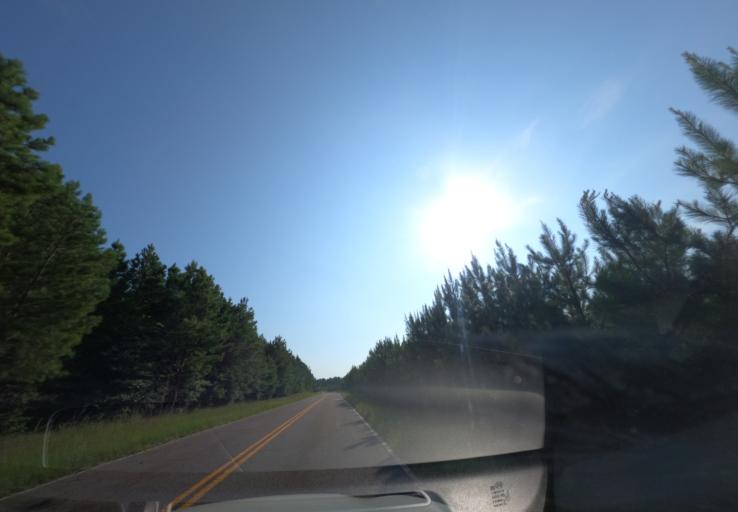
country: US
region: South Carolina
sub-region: Edgefield County
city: Edgefield
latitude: 33.7585
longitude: -81.9514
